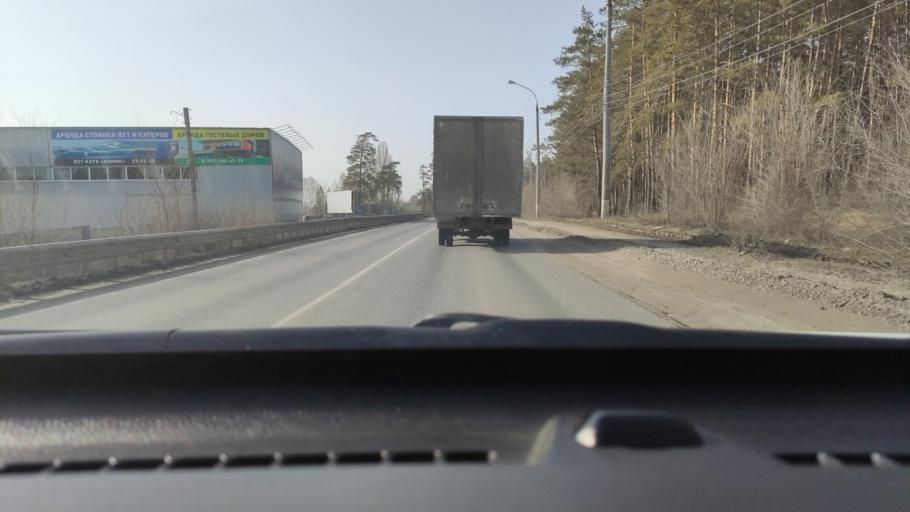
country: RU
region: Samara
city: Tol'yatti
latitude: 53.4747
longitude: 49.3275
